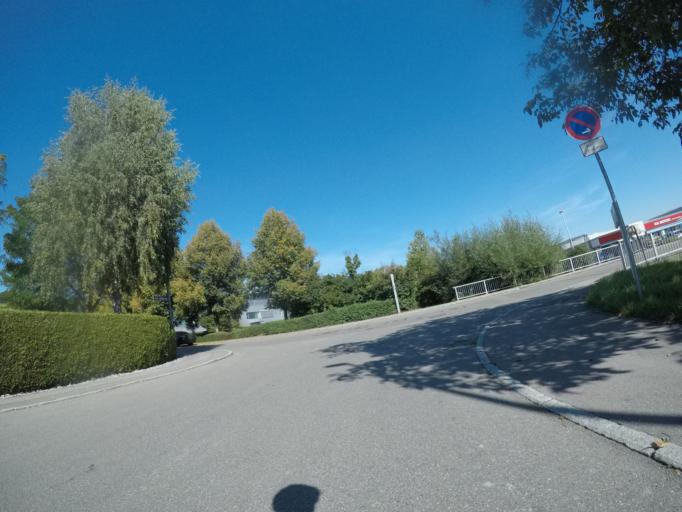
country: DE
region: Baden-Wuerttemberg
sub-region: Tuebingen Region
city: Wannweil
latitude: 48.4879
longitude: 9.1499
